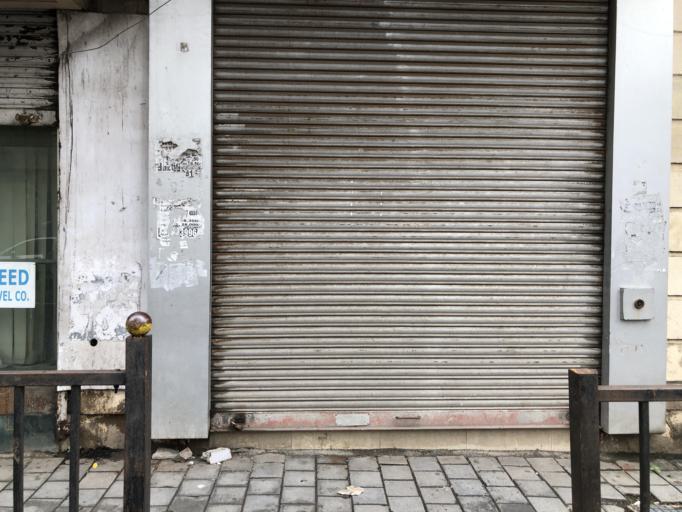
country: IN
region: Maharashtra
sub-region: Raigarh
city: Uran
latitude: 18.9449
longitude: 72.8280
